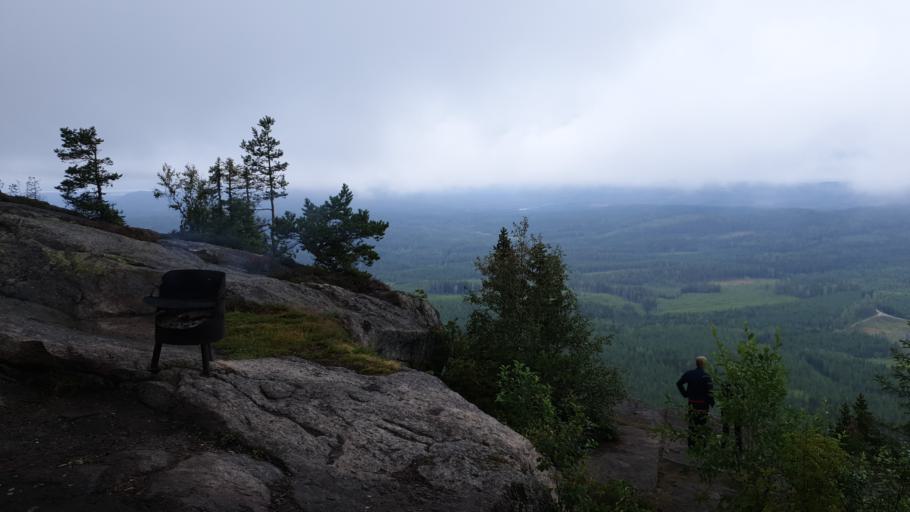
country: SE
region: Gaevleborg
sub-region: Hudiksvalls Kommun
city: Sorforsa
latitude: 61.6472
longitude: 16.7640
